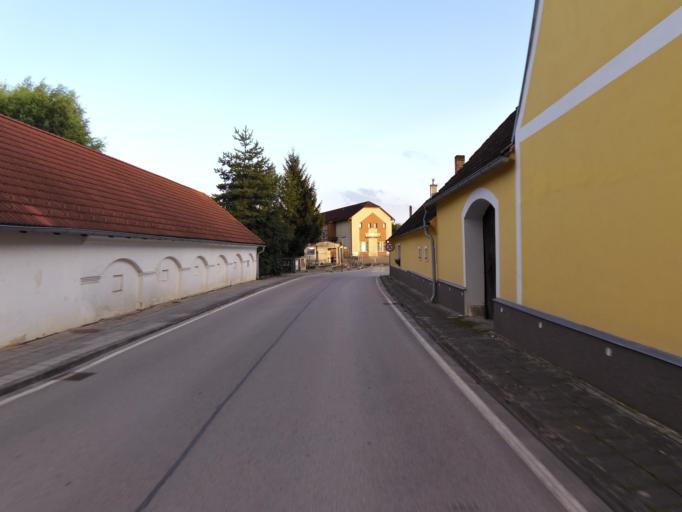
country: CZ
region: Jihocesky
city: Chlum u Trebone
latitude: 48.9516
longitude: 14.9152
